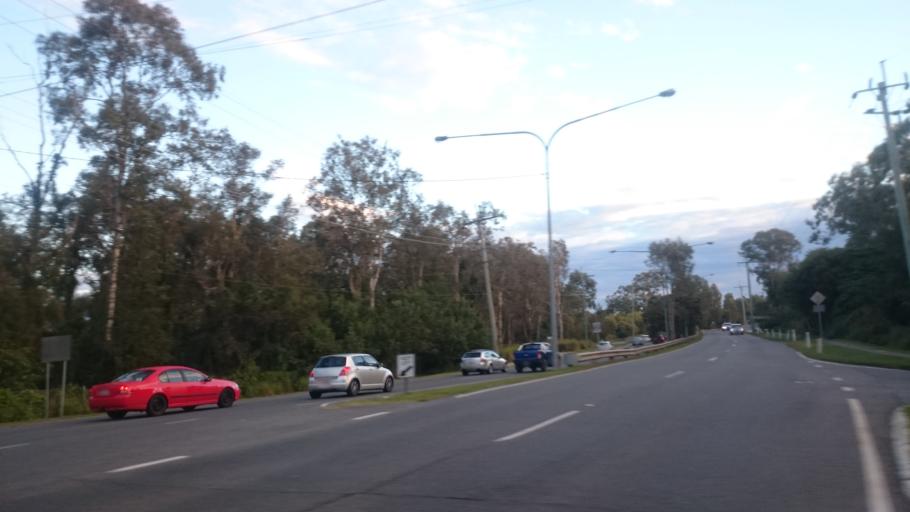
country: AU
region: Queensland
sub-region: Brisbane
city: Wynnum West
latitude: -27.4705
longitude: 153.1342
